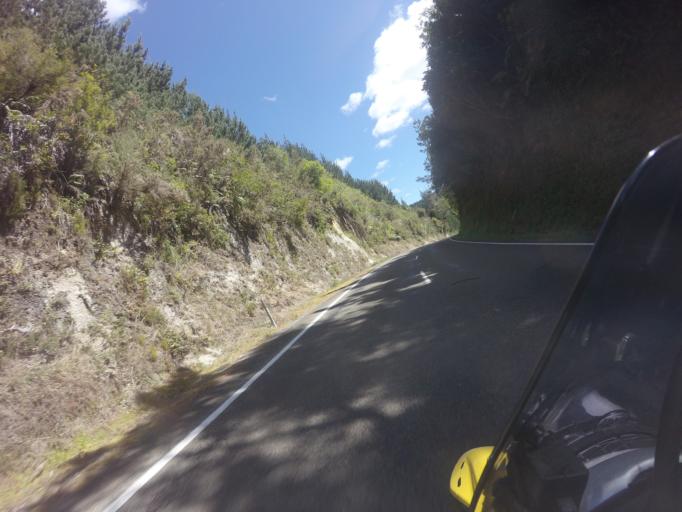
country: NZ
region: Bay of Plenty
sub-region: Kawerau District
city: Kawerau
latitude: -38.1690
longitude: 176.8177
